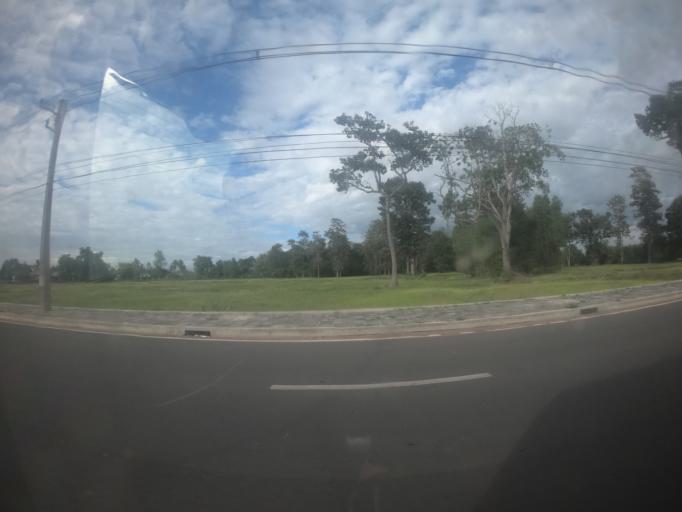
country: TH
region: Surin
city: Prasat
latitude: 14.6148
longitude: 103.4168
